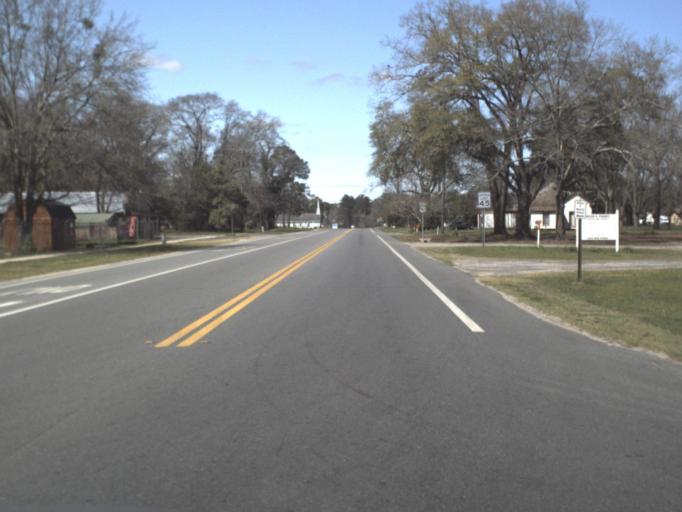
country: US
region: Florida
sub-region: Gadsden County
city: Gretna
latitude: 30.6154
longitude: -84.6617
